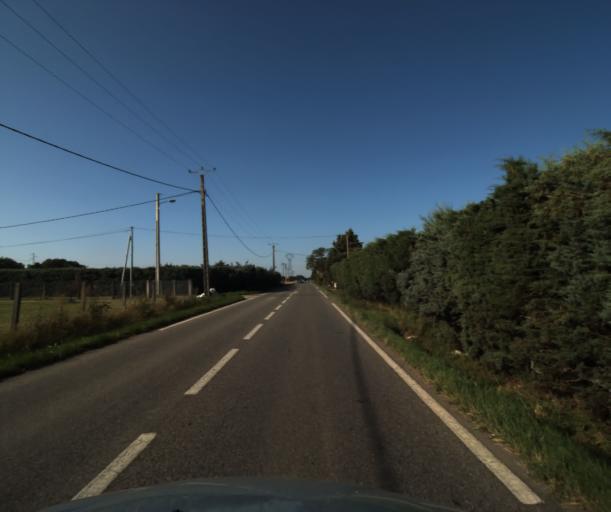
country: FR
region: Midi-Pyrenees
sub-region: Departement de la Haute-Garonne
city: Lagardelle-sur-Leze
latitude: 43.4238
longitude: 1.3760
